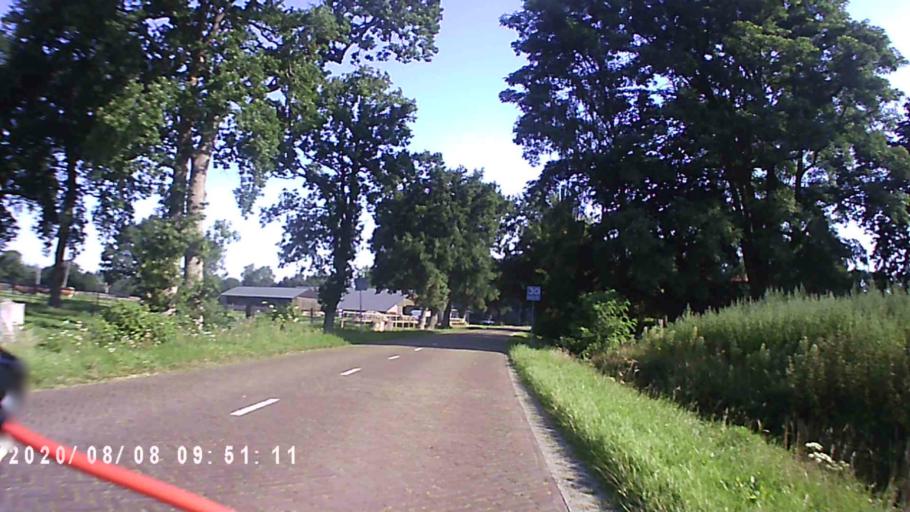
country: NL
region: Groningen
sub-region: Gemeente Leek
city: Leek
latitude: 53.0879
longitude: 6.3874
